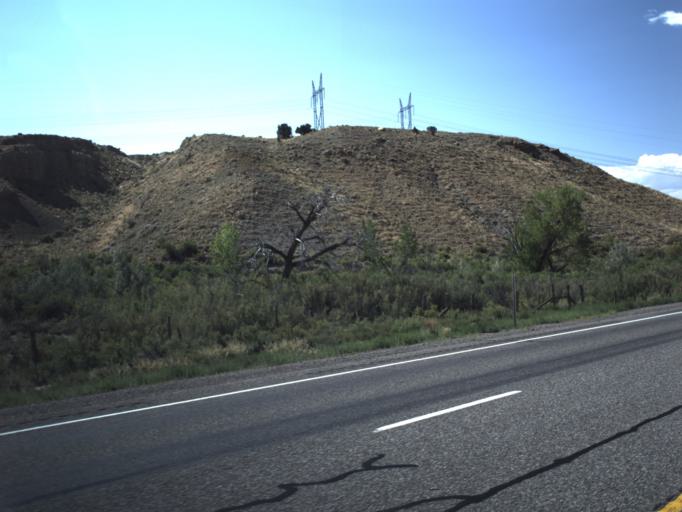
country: US
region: Utah
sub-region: Emery County
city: Ferron
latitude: 38.8868
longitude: -111.2839
